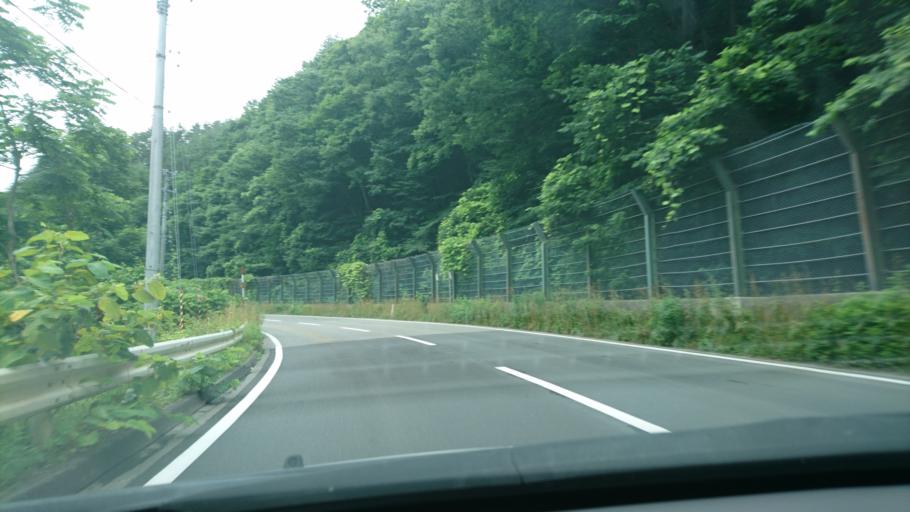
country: JP
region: Iwate
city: Miyako
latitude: 39.9751
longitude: 141.8627
